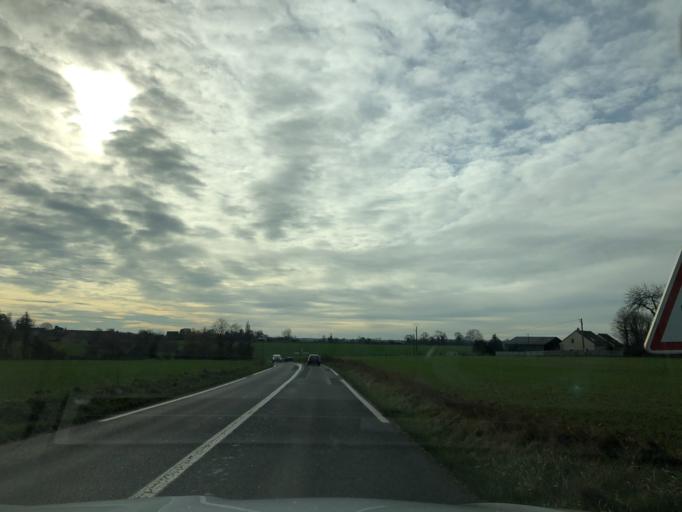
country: FR
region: Lower Normandy
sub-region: Departement du Calvados
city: Beuville
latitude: 49.2519
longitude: -0.3289
